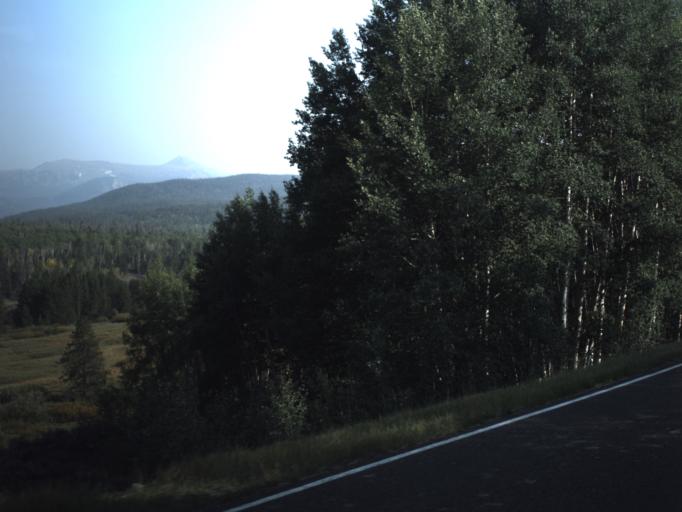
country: US
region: Wyoming
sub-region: Uinta County
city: Evanston
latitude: 40.8491
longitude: -110.8470
